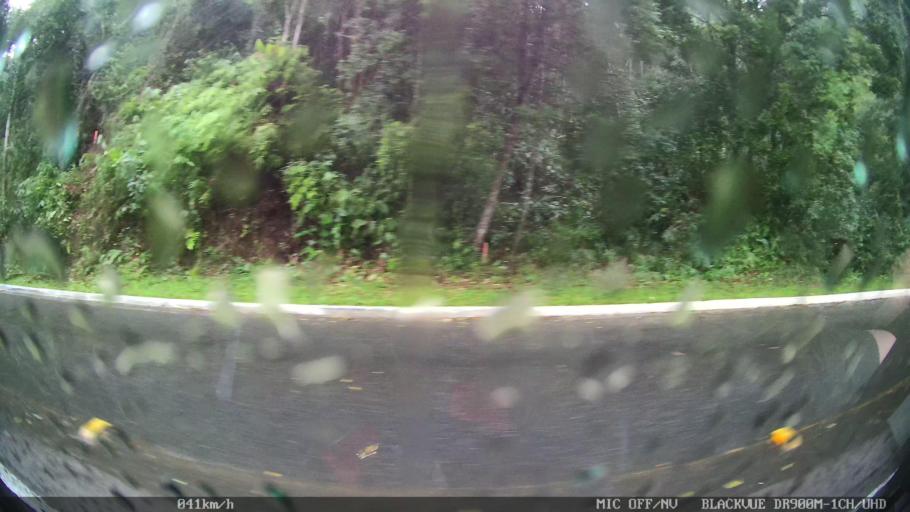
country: BR
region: Santa Catarina
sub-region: Itajai
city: Itajai
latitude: -26.9344
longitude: -48.6389
